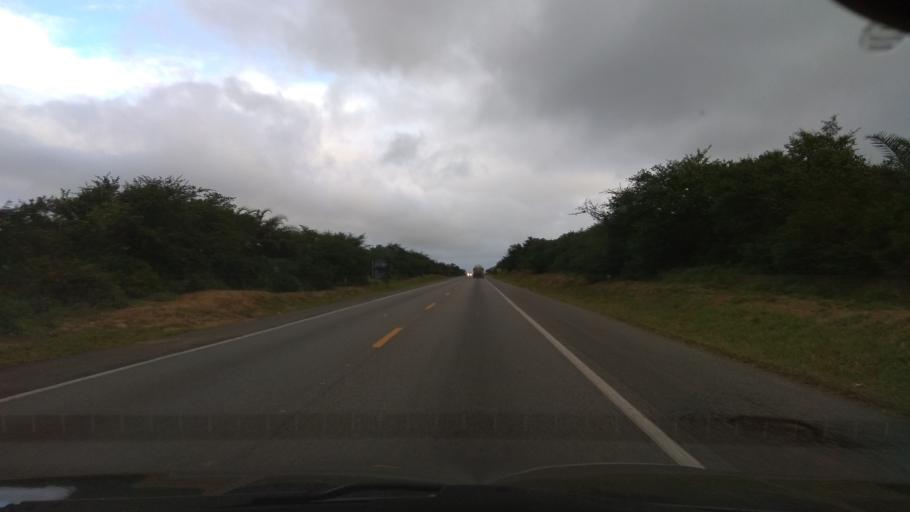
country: BR
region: Bahia
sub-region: Jaguaquara
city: Jaguaquara
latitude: -13.3406
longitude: -40.0167
